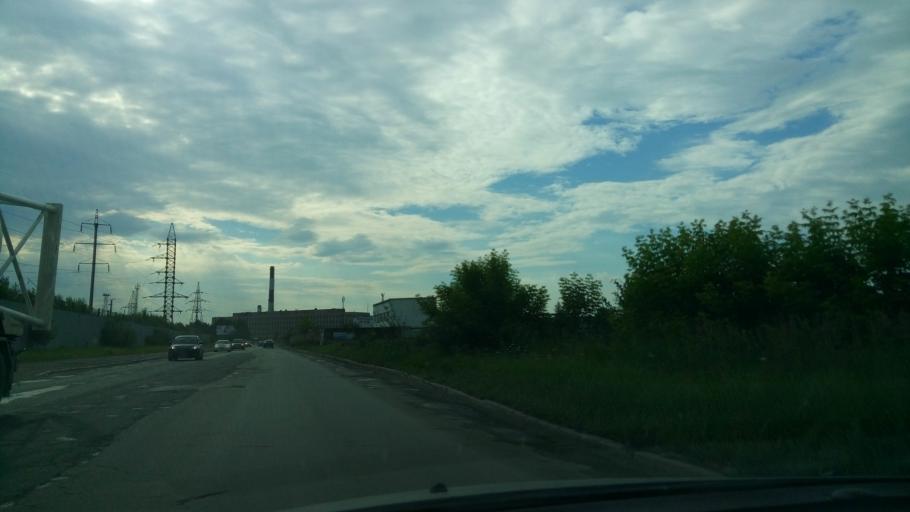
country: RU
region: Sverdlovsk
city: Yekaterinburg
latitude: 56.8868
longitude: 60.6597
